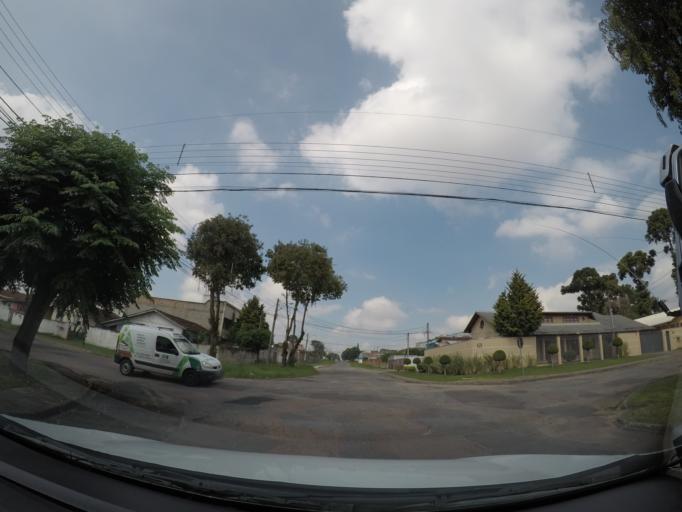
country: BR
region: Parana
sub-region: Curitiba
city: Curitiba
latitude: -25.4790
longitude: -49.2596
